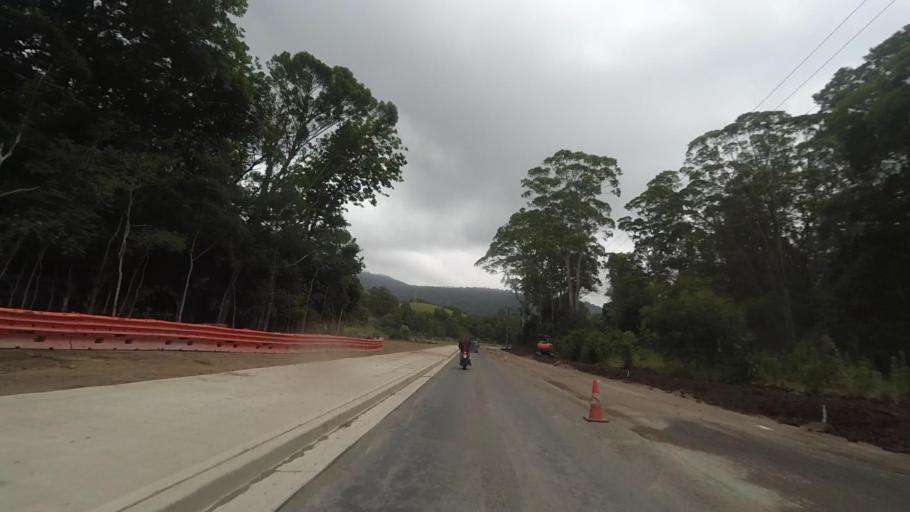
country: AU
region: New South Wales
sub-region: Wollongong
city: Cordeaux Heights
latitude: -34.4342
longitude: 150.8320
